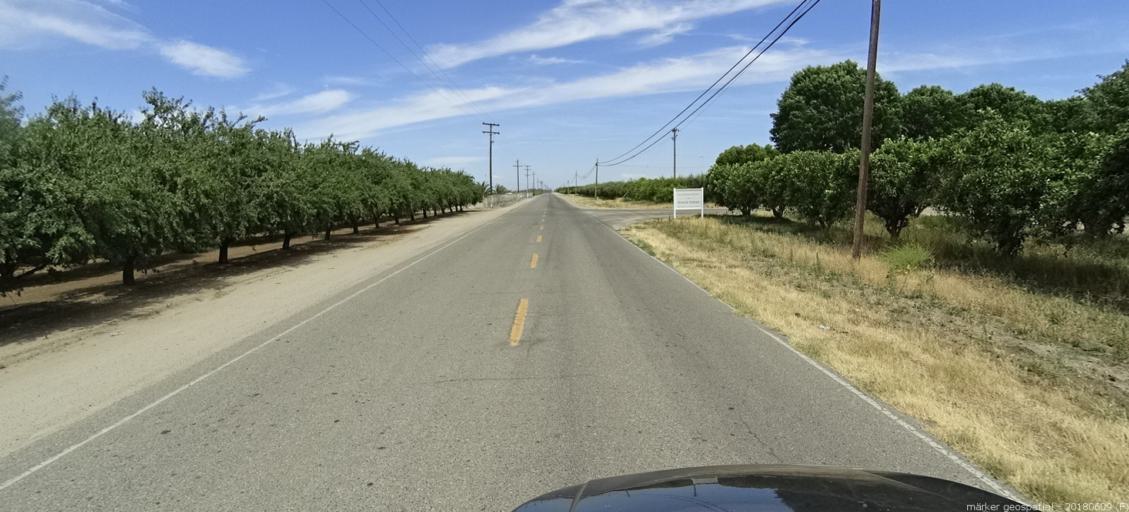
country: US
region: California
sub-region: Madera County
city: Parkwood
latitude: 36.9093
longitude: -120.0775
